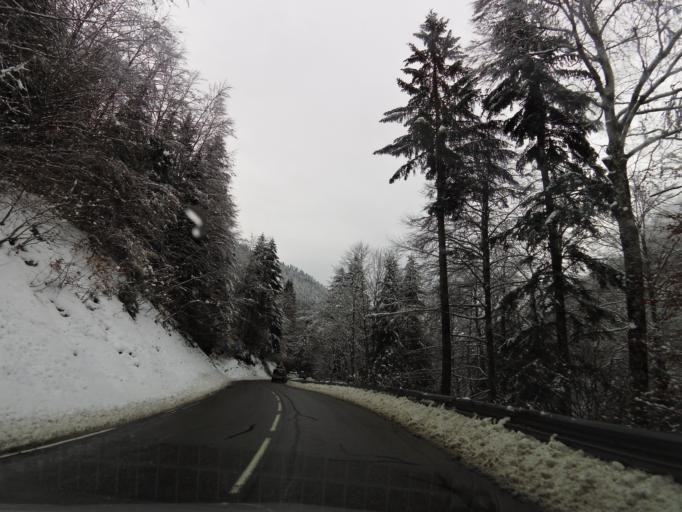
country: FR
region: Rhone-Alpes
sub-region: Departement de la Haute-Savoie
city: Taninges
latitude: 46.1297
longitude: 6.6237
